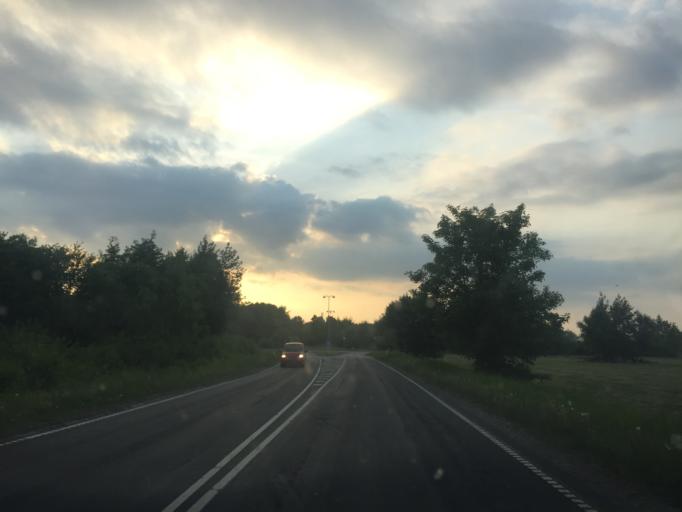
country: DK
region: South Denmark
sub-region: Odense Kommune
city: Neder Holluf
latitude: 55.3579
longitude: 10.4765
